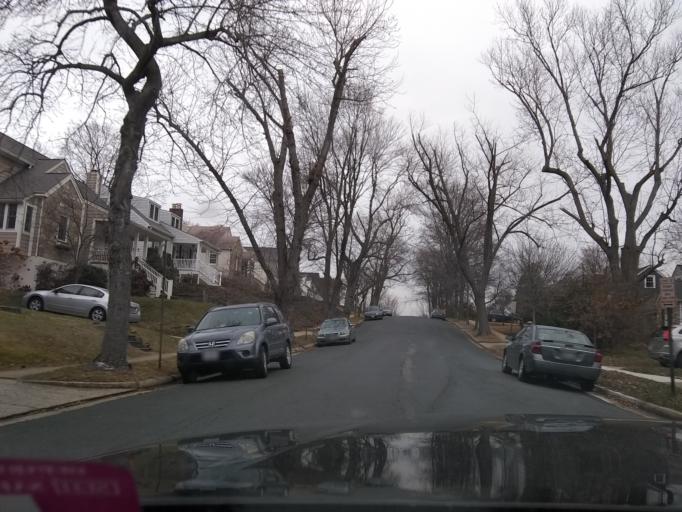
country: US
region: Virginia
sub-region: Arlington County
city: Arlington
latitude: 38.8898
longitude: -77.1252
